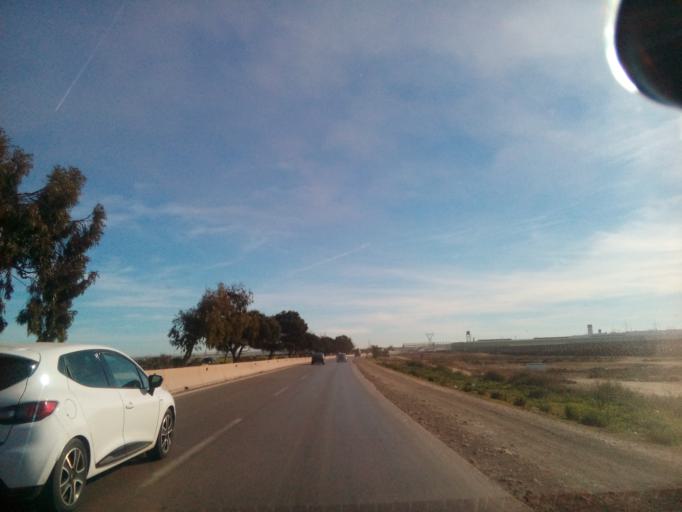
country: DZ
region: Oran
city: Ain el Bya
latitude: 35.7795
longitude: -0.2698
